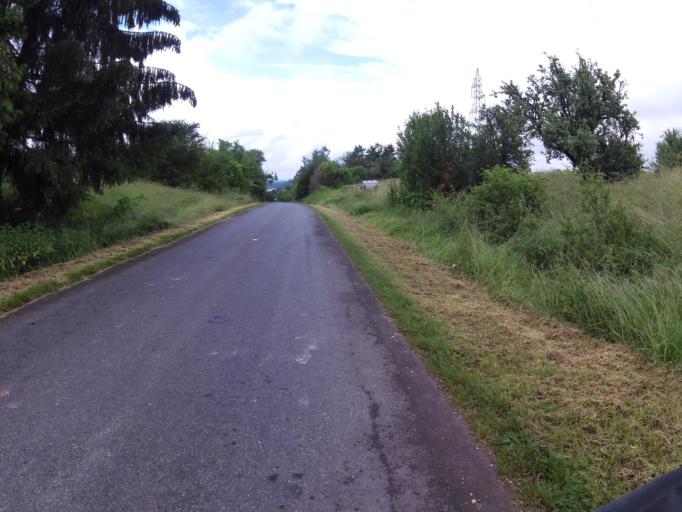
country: FR
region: Champagne-Ardenne
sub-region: Departement de la Marne
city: Sermaize-les-Bains
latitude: 48.7779
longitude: 4.9202
